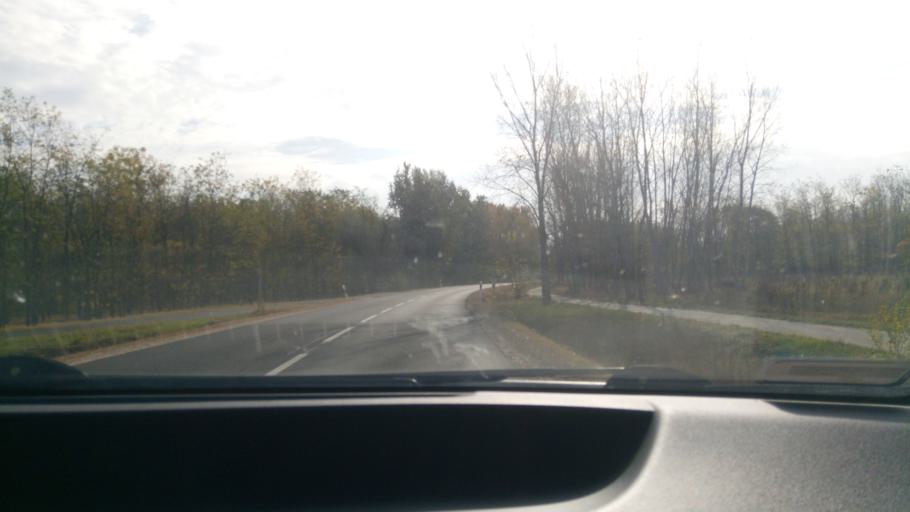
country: HU
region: Bacs-Kiskun
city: Jaszszentlaszlo
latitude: 46.5570
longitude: 19.7475
